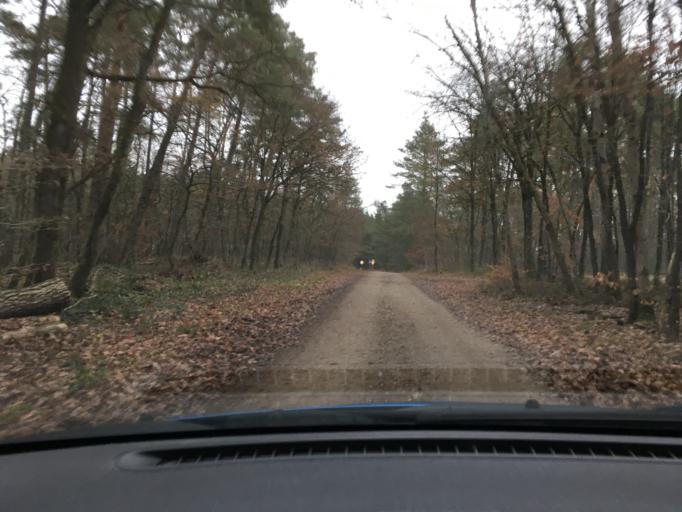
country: DE
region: Lower Saxony
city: Betzendorf
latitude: 53.1471
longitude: 10.2837
